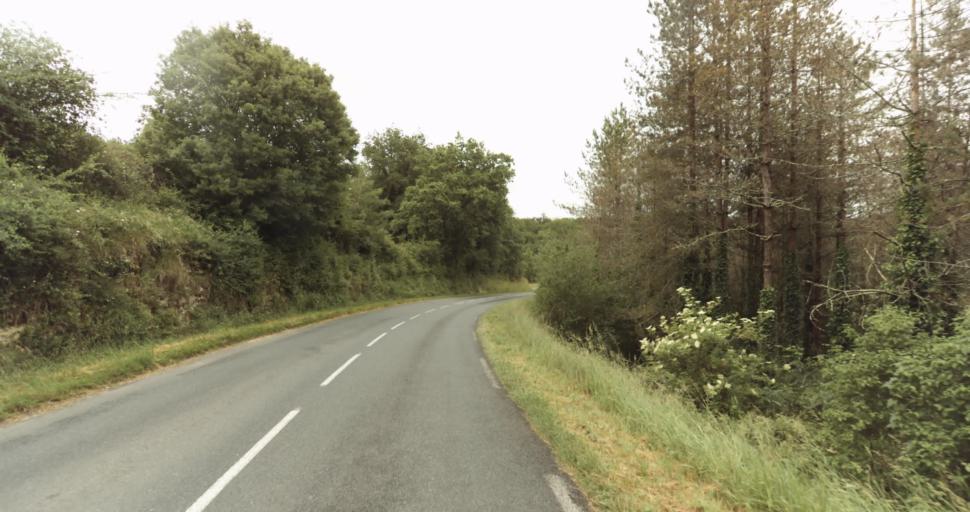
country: FR
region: Aquitaine
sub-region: Departement de la Dordogne
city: Beaumont-du-Perigord
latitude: 44.7674
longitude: 0.7885
